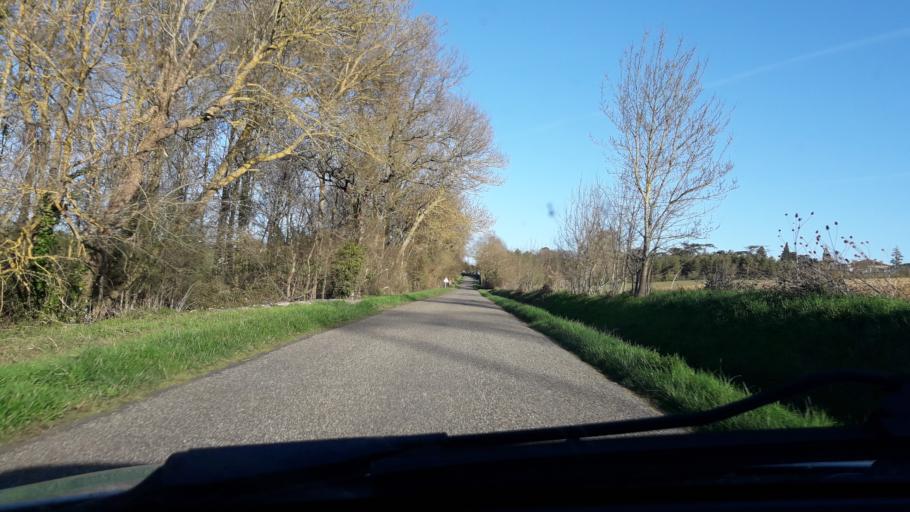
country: FR
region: Midi-Pyrenees
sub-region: Departement du Gers
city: Pujaudran
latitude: 43.6215
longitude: 1.0220
